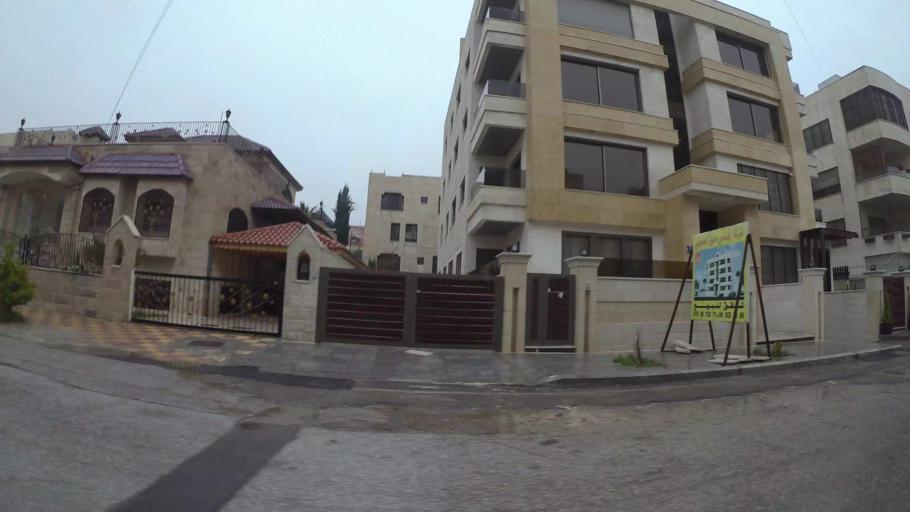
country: JO
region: Amman
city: Wadi as Sir
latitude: 31.9711
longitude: 35.8657
